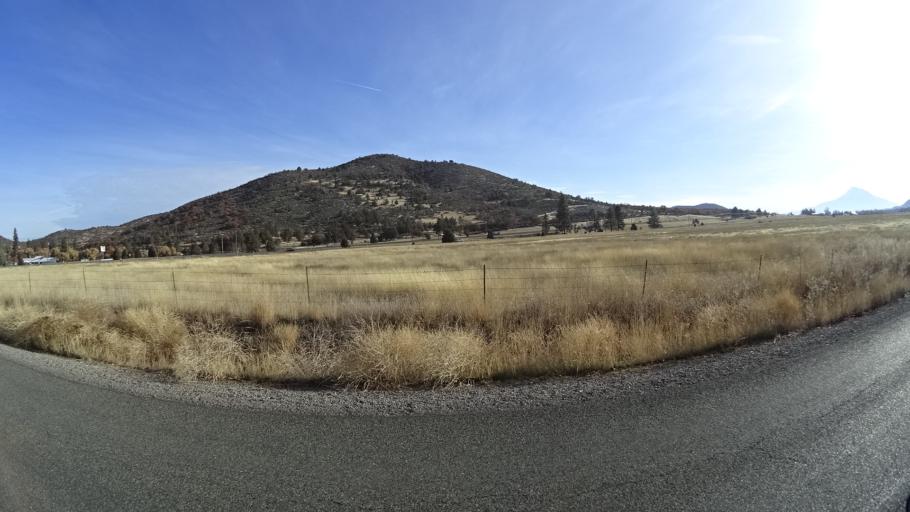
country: US
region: California
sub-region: Siskiyou County
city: Yreka
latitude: 41.6805
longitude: -122.6346
